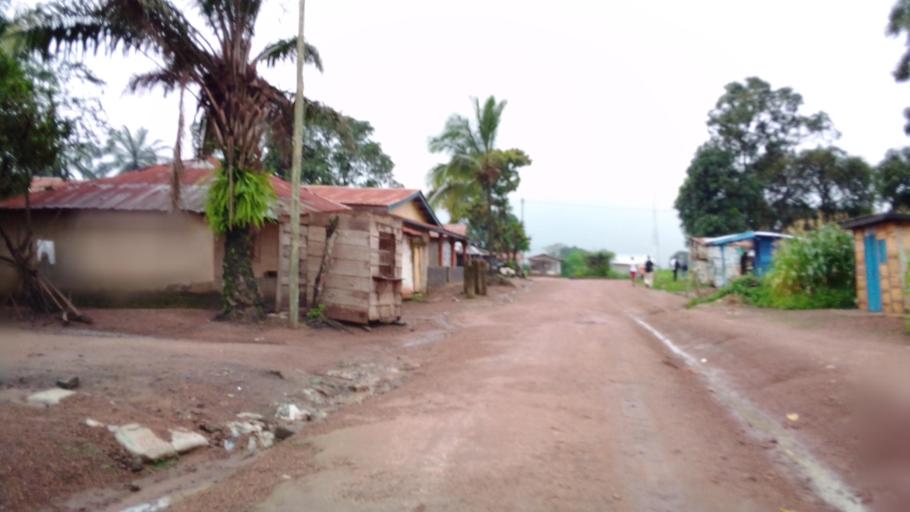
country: SL
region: Eastern Province
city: Kenema
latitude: 7.8956
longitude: -11.1726
